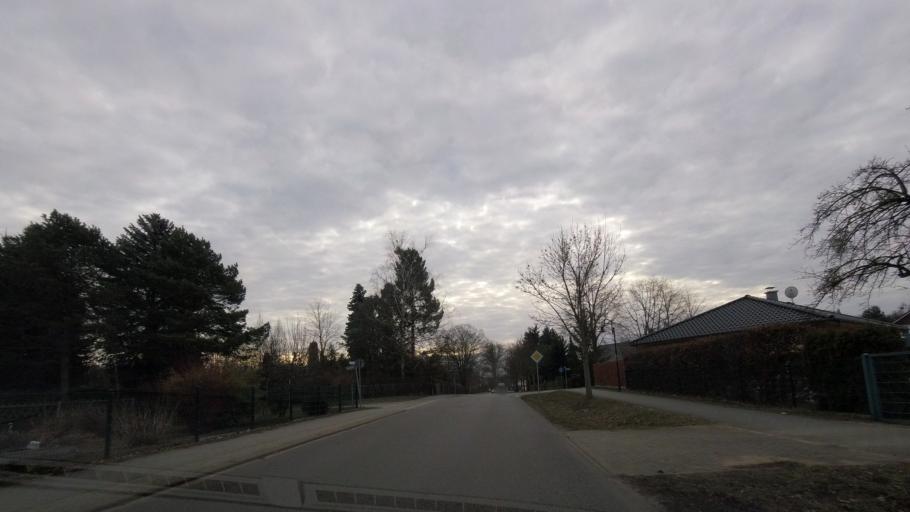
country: DE
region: Brandenburg
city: Woltersdorf
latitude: 52.4570
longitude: 13.7359
